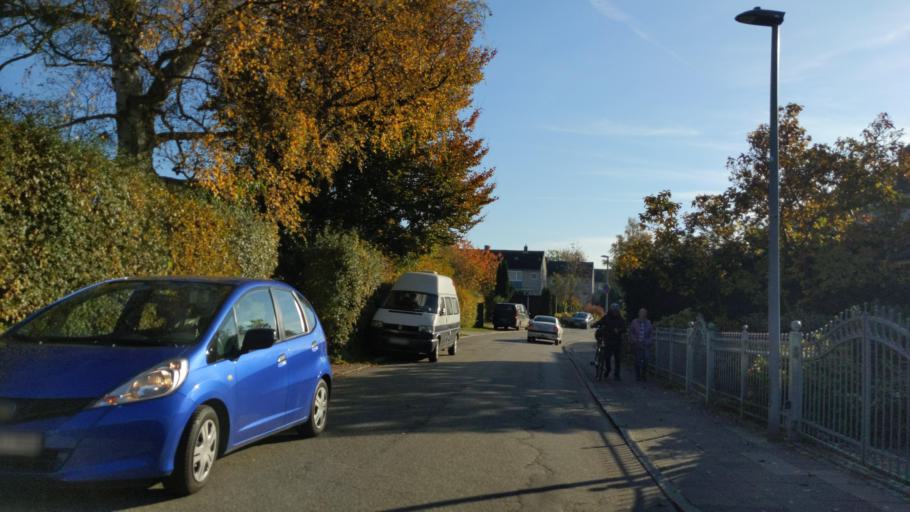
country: DE
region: Schleswig-Holstein
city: Eutin
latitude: 54.1275
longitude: 10.6168
